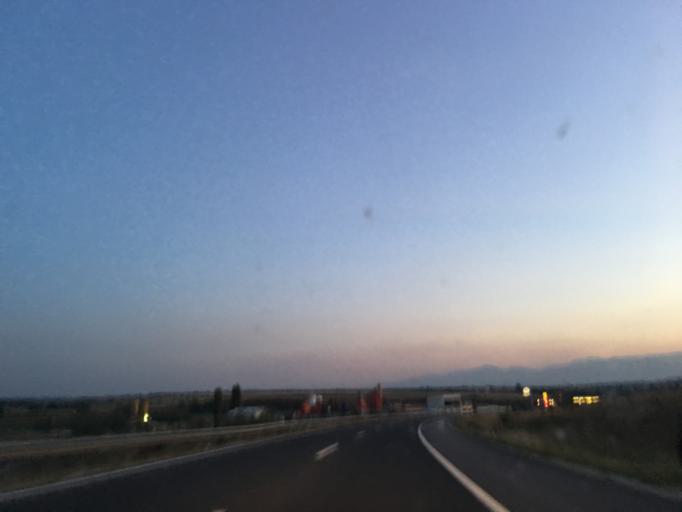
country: MK
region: Kumanovo
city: Romanovce
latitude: 42.0811
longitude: 21.7027
